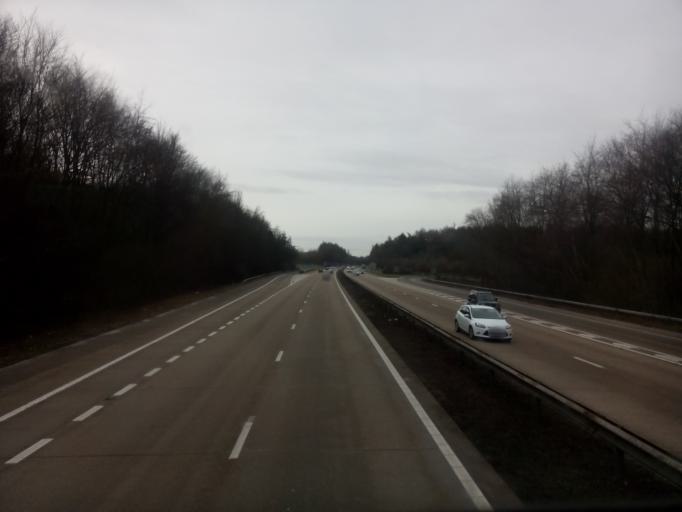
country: GB
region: England
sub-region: Hampshire
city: Kings Worthy
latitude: 51.1208
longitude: -1.2524
